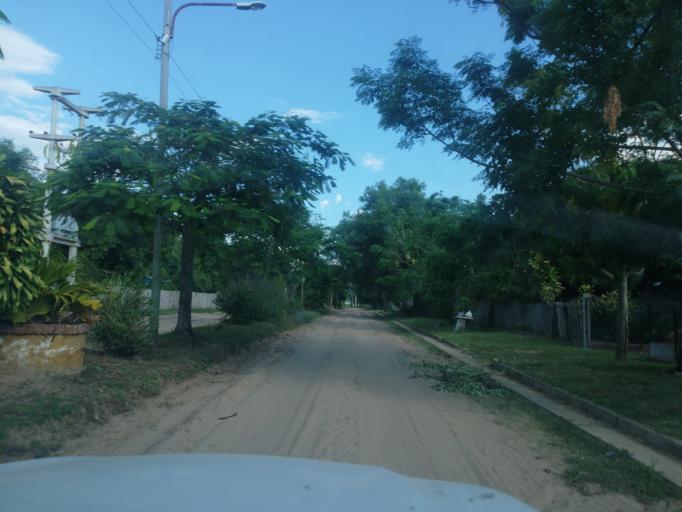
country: AR
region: Corrientes
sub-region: Departamento de San Miguel
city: San Miguel
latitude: -28.0003
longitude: -57.5943
